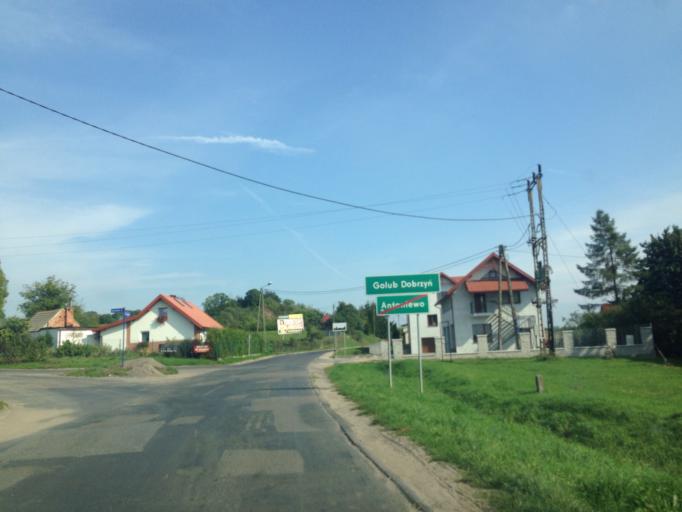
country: PL
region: Kujawsko-Pomorskie
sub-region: Powiat golubsko-dobrzynski
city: Golub-Dobrzyn
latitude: 53.1112
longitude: 19.0417
